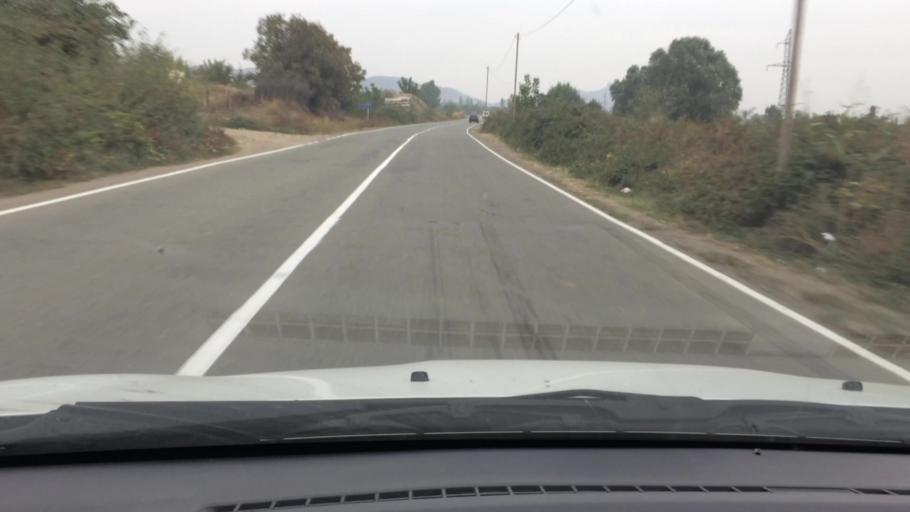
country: GE
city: Naghvarevi
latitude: 41.3109
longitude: 44.7923
